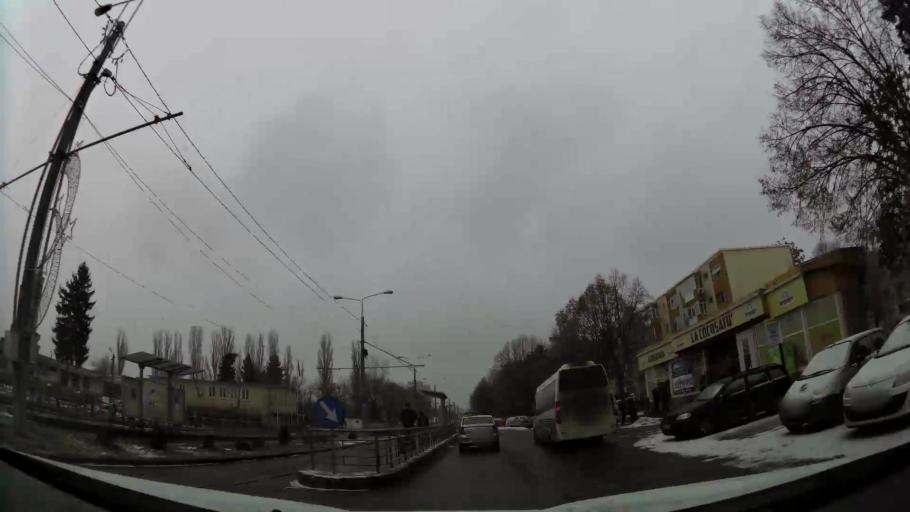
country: RO
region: Prahova
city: Ploiesti
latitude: 44.9604
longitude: 26.0099
